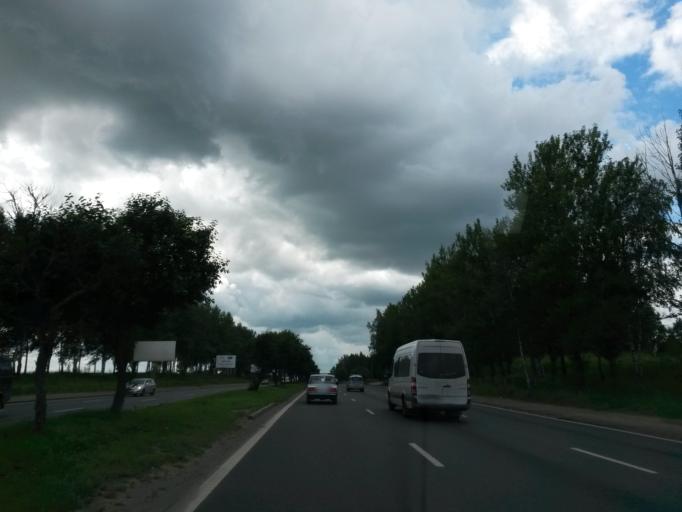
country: RU
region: Jaroslavl
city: Yaroslavl
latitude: 57.5702
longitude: 39.8366
